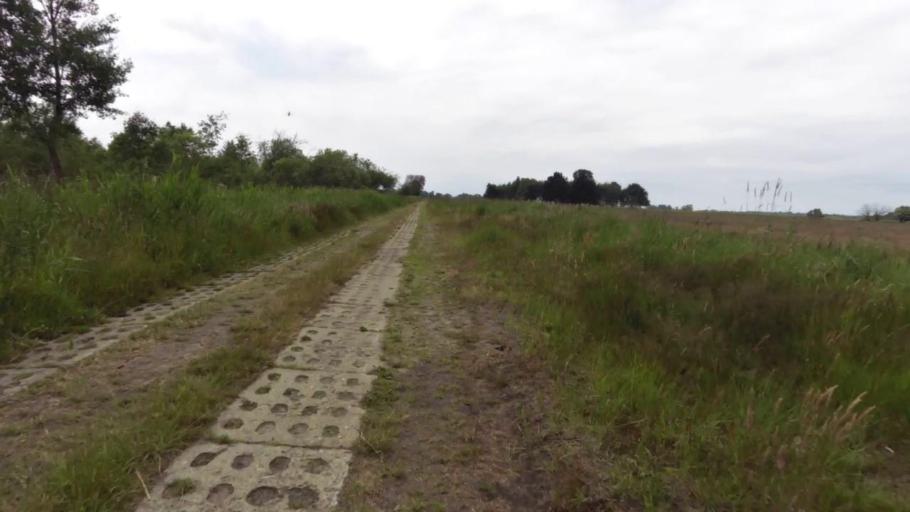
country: PL
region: West Pomeranian Voivodeship
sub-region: Powiat goleniowski
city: Stepnica
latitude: 53.7162
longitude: 14.5801
